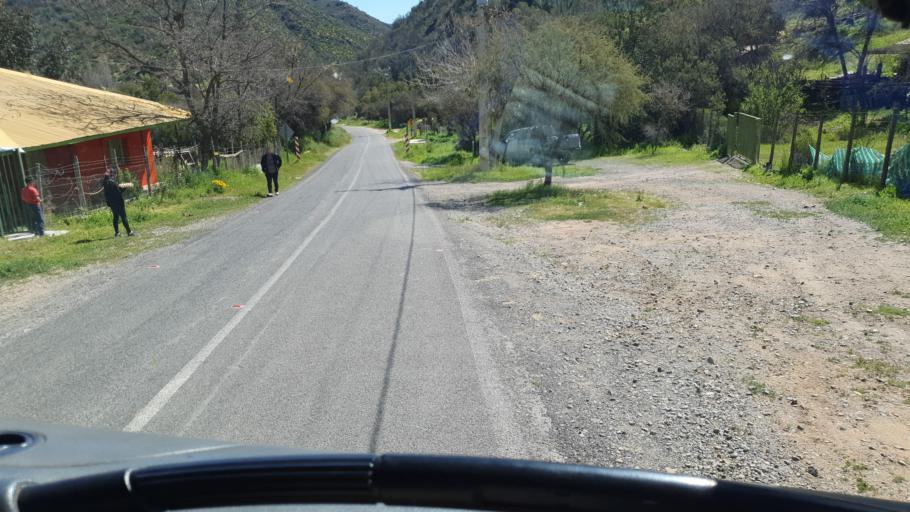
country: CL
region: Valparaiso
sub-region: Provincia de Marga Marga
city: Limache
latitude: -33.1841
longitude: -71.1053
